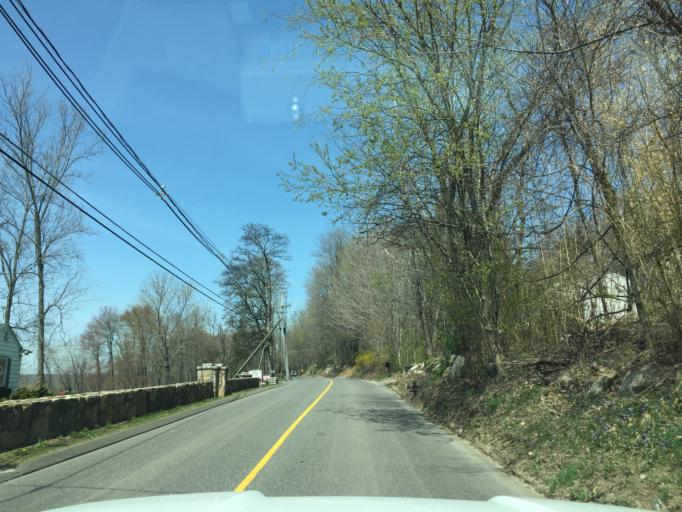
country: US
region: Connecticut
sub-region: Fairfield County
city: Bethel
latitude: 41.4060
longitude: -73.4022
